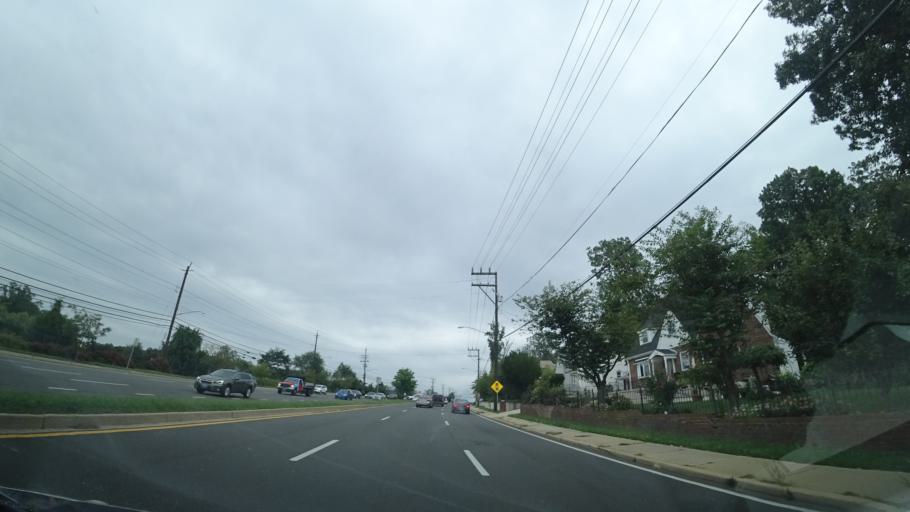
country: US
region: Maryland
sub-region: Montgomery County
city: White Oak
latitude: 39.0319
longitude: -76.9850
